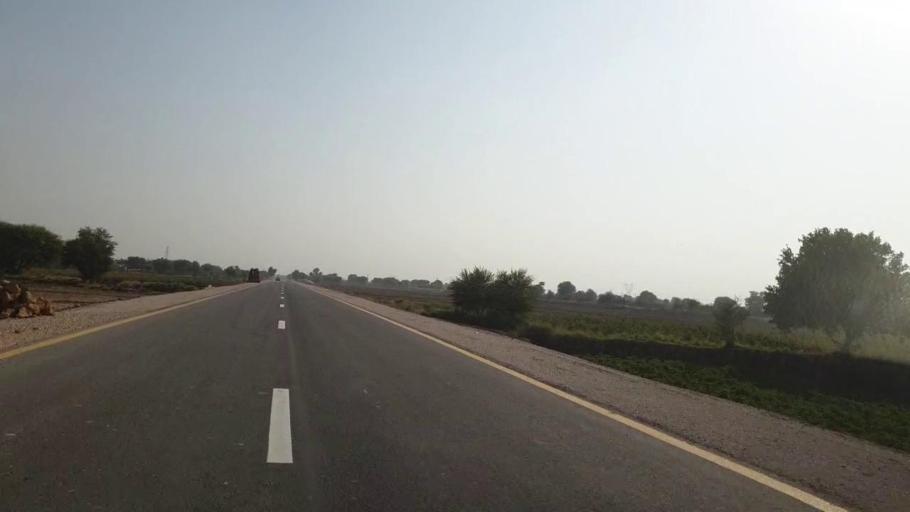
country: PK
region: Sindh
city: Bhan
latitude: 26.4932
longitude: 67.7800
